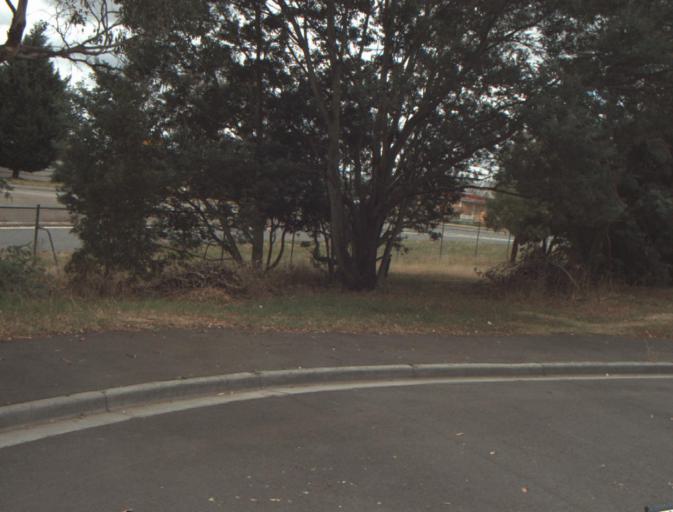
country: AU
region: Tasmania
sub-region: Launceston
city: West Launceston
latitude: -41.4546
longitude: 147.1431
